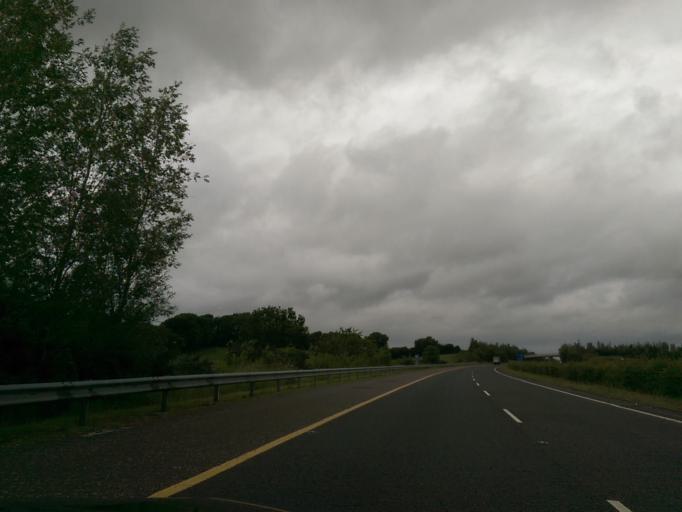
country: IE
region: Munster
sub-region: An Clar
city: Newmarket on Fergus
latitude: 52.7332
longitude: -8.8879
